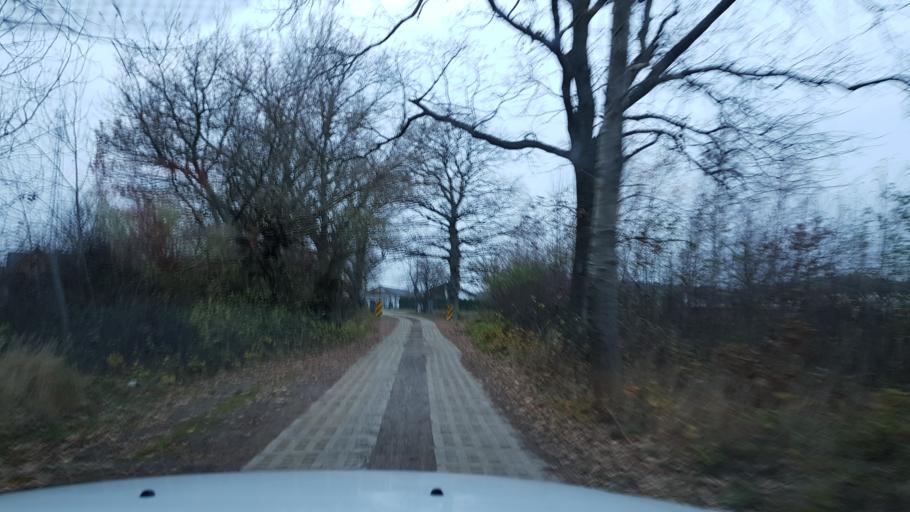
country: PL
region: West Pomeranian Voivodeship
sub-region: Powiat slawienski
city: Darlowo
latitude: 54.5098
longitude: 16.4868
